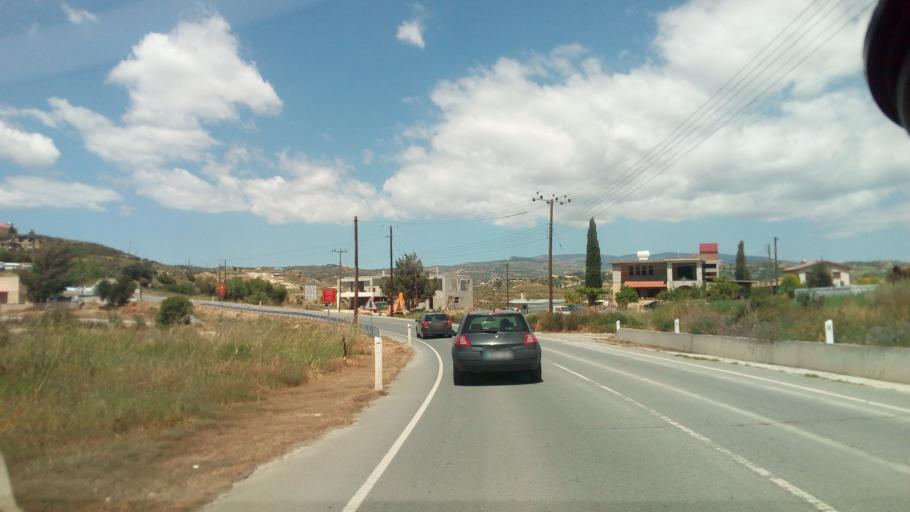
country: CY
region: Limassol
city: Pachna
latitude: 34.7782
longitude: 32.8330
